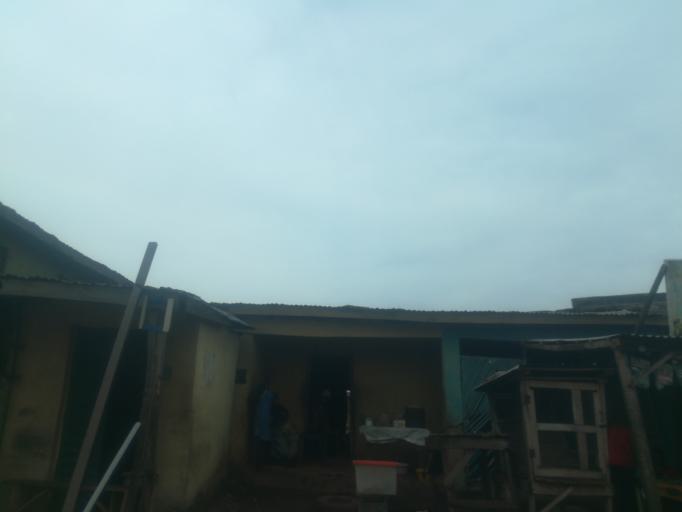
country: NG
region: Oyo
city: Ibadan
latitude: 7.3737
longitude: 3.9314
